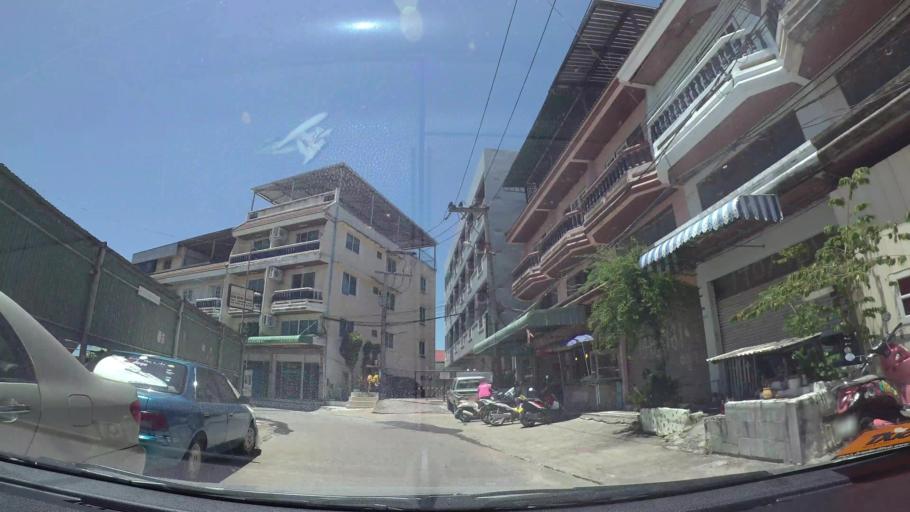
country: TH
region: Chon Buri
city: Phatthaya
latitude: 12.9191
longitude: 100.8948
